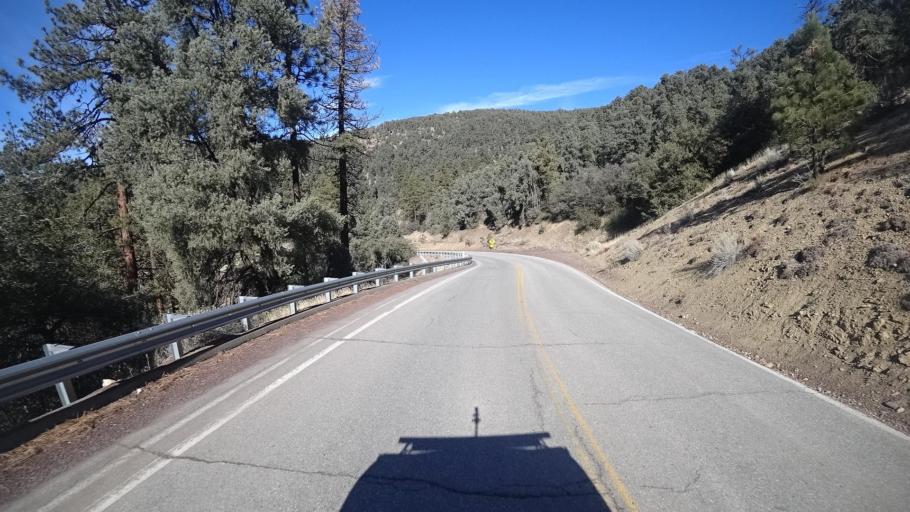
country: US
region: California
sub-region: Kern County
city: Pine Mountain Club
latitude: 34.8459
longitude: -119.0840
